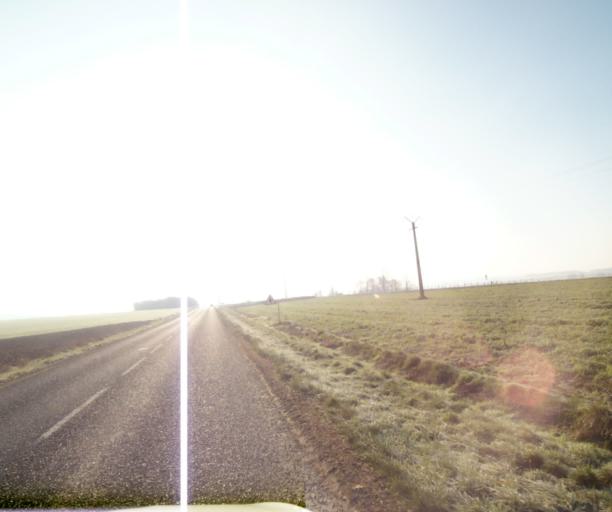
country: FR
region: Champagne-Ardenne
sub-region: Departement de la Haute-Marne
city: Montier-en-Der
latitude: 48.4970
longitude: 4.7531
